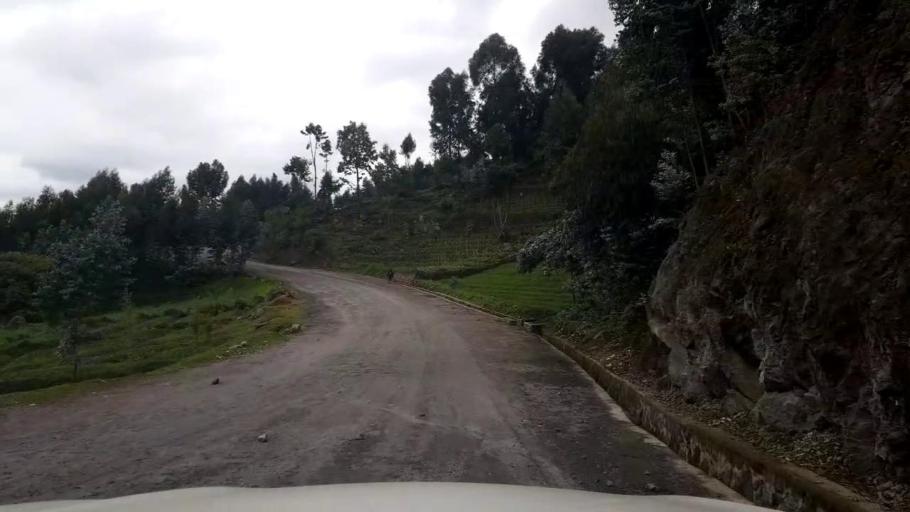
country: RW
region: Northern Province
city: Musanze
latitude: -1.5222
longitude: 29.5338
